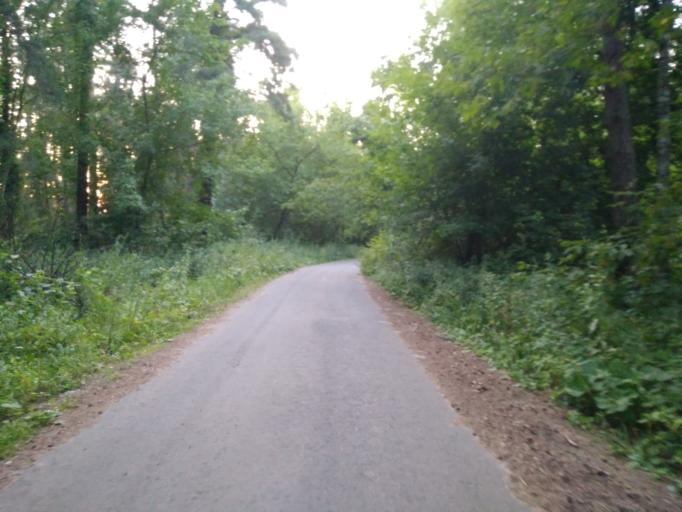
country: RU
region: Moskovskaya
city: Zhukovskiy
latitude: 55.5795
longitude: 38.1158
